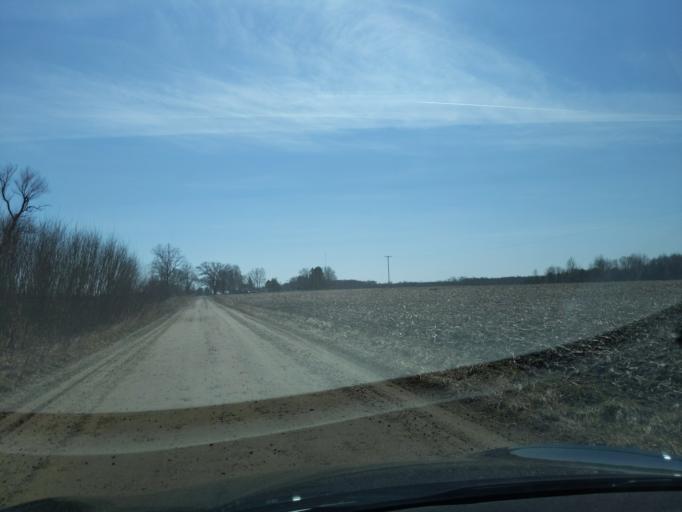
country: US
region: Michigan
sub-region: Ionia County
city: Lake Odessa
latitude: 42.7182
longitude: -85.0539
